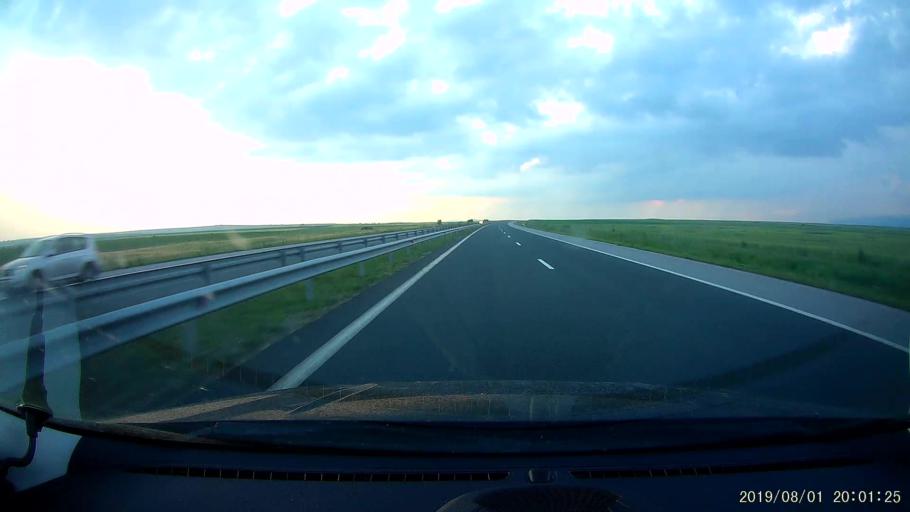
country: BG
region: Yambol
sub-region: Obshtina Straldzha
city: Straldzha
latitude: 42.5560
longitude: 26.6663
